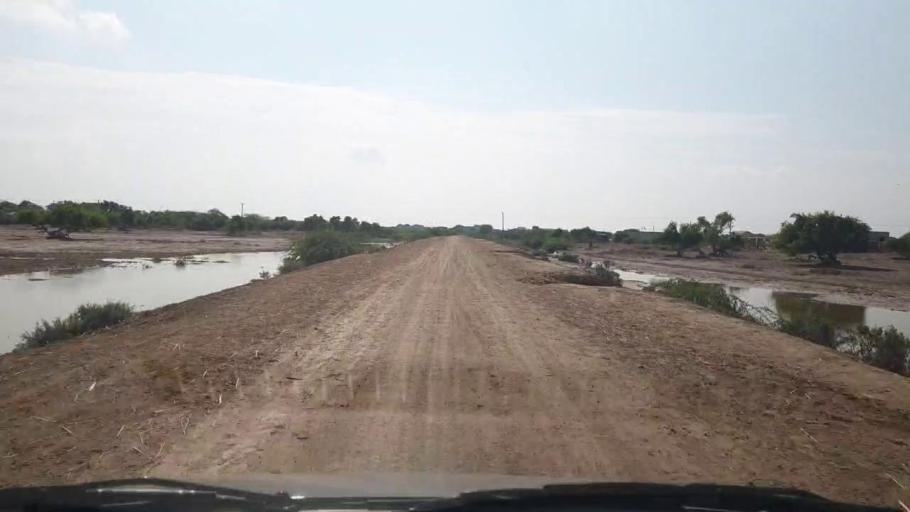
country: PK
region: Sindh
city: Badin
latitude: 24.4811
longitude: 68.6126
